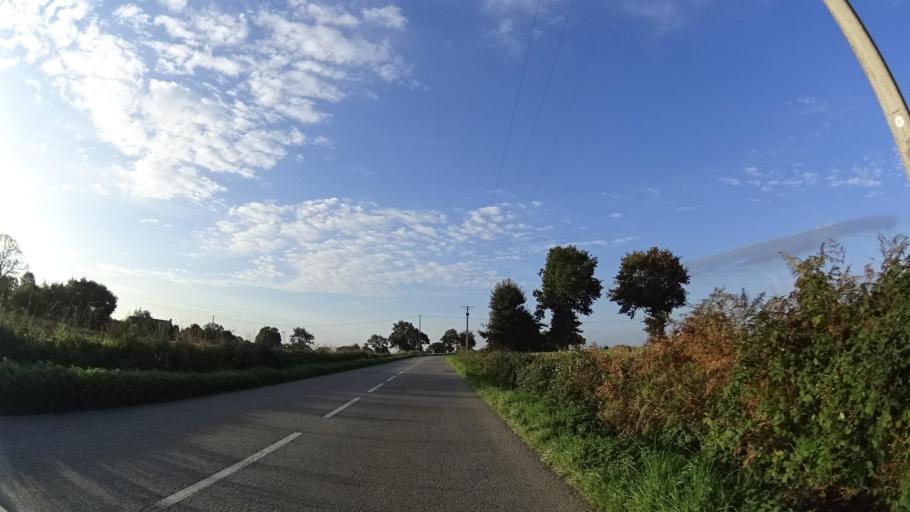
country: FR
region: Brittany
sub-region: Departement des Cotes-d'Armor
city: Plouasne
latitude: 48.2867
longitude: -1.9694
